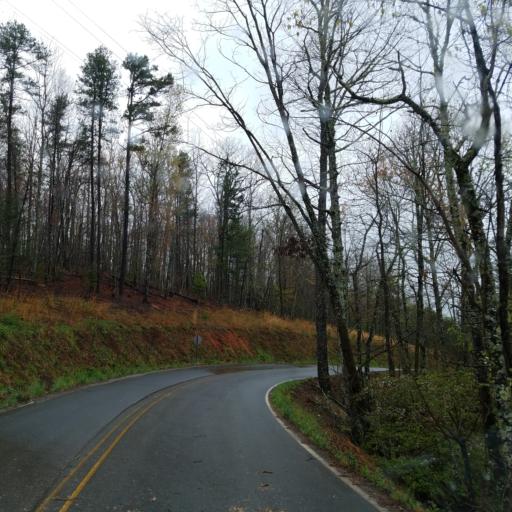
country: US
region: Georgia
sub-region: Fannin County
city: Blue Ridge
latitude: 34.8451
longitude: -84.2340
